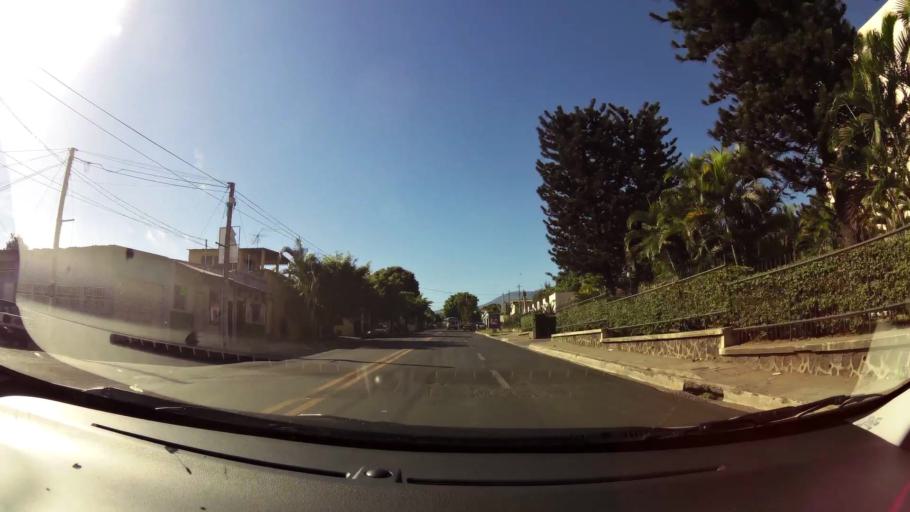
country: SV
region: Santa Ana
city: Santa Ana
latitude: 13.9740
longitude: -89.5718
